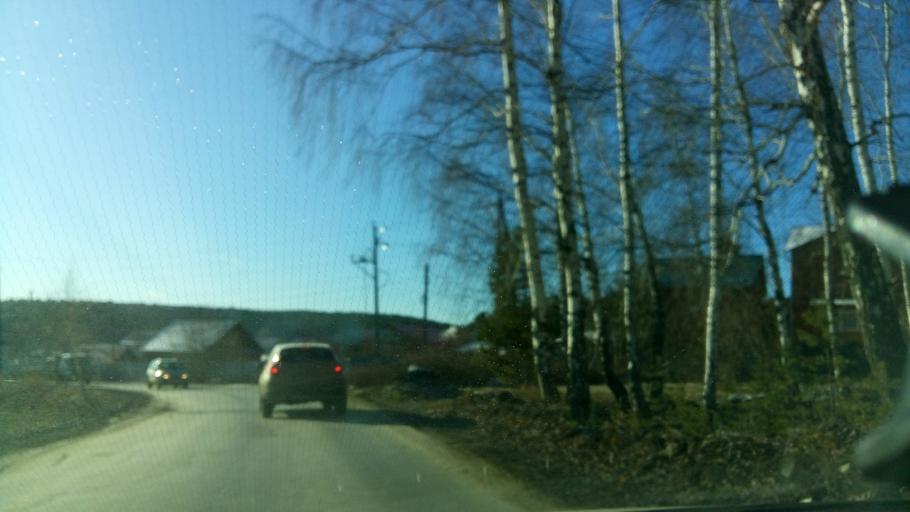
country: RU
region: Sverdlovsk
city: Gornyy Shchit
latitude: 56.7169
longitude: 60.5159
